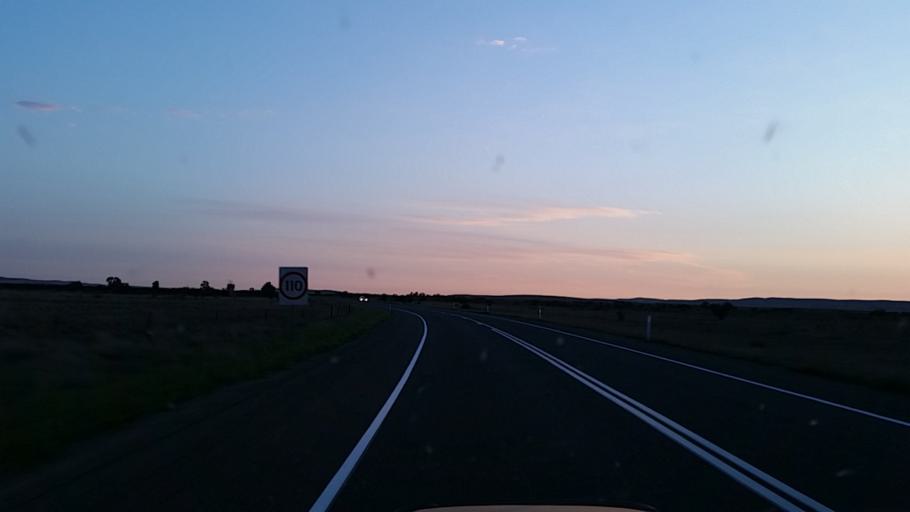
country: AU
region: South Australia
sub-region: Peterborough
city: Peterborough
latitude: -33.1553
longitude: 138.9211
